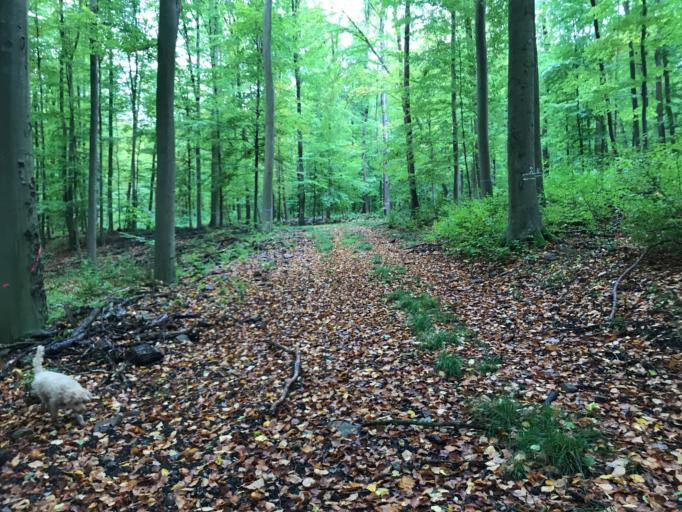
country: DE
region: Hesse
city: Witzenhausen
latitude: 51.3081
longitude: 9.8509
